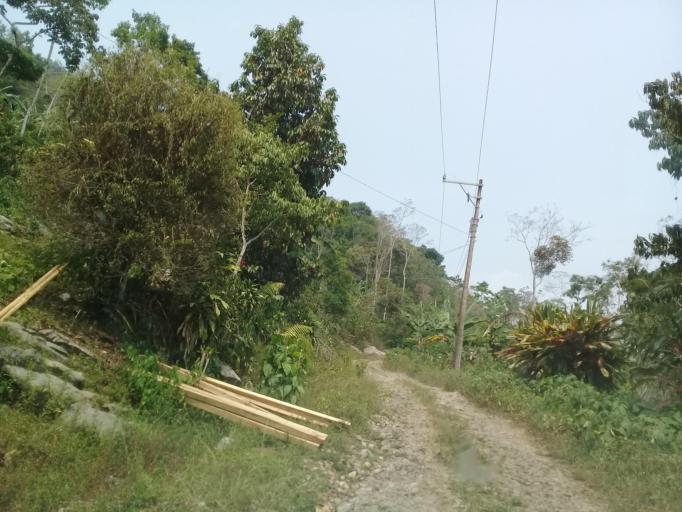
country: MX
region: Veracruz
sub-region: Tezonapa
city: Laguna Chica (Pueblo Nuevo)
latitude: 18.5820
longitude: -96.7540
